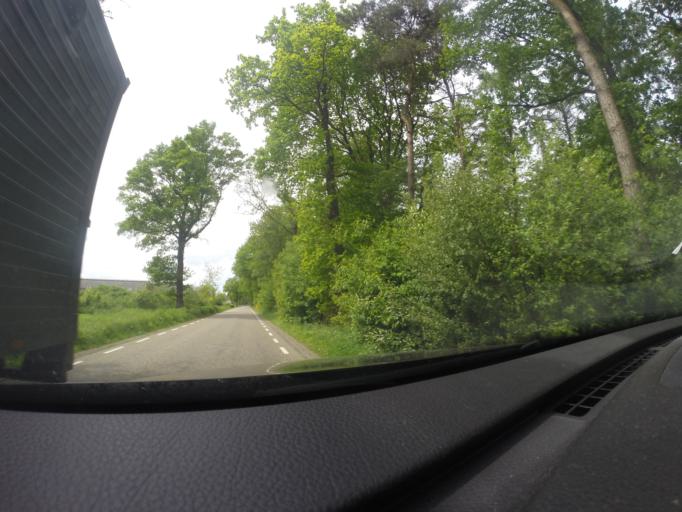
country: NL
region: Overijssel
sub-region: Gemeente Raalte
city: Raalte
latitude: 52.3041
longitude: 6.3064
